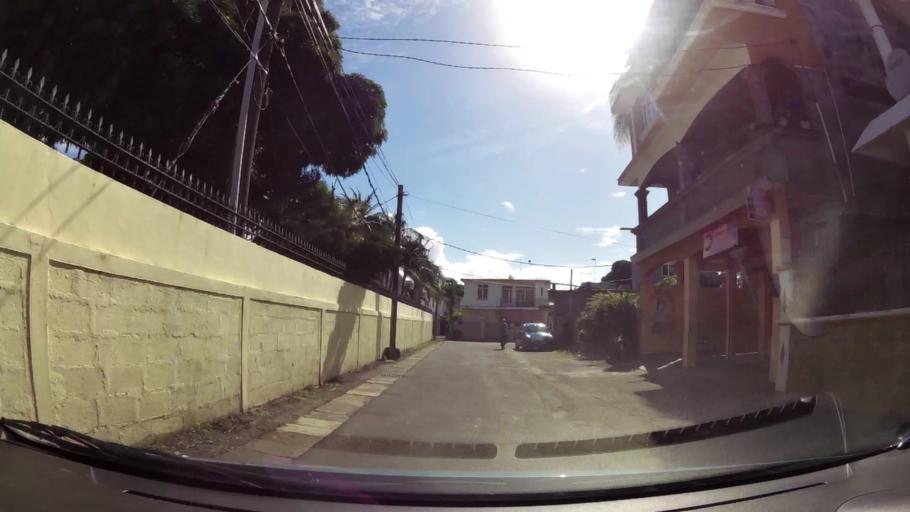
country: MU
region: Grand Port
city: Mahebourg
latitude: -20.4110
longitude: 57.7035
